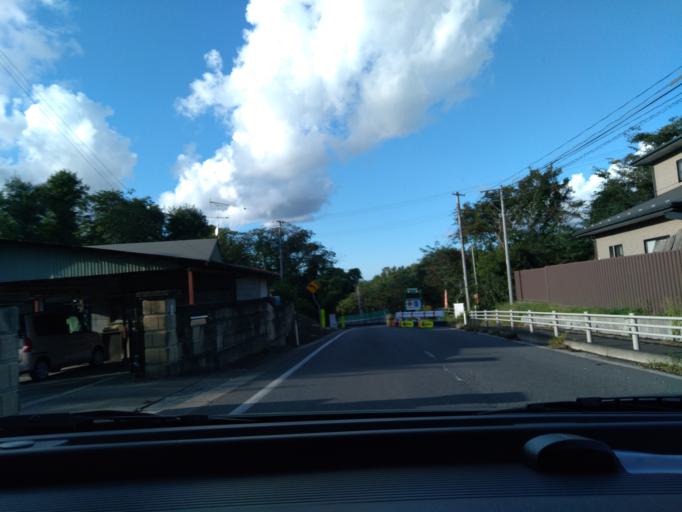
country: JP
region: Iwate
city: Ichinoseki
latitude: 38.7819
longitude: 141.2179
